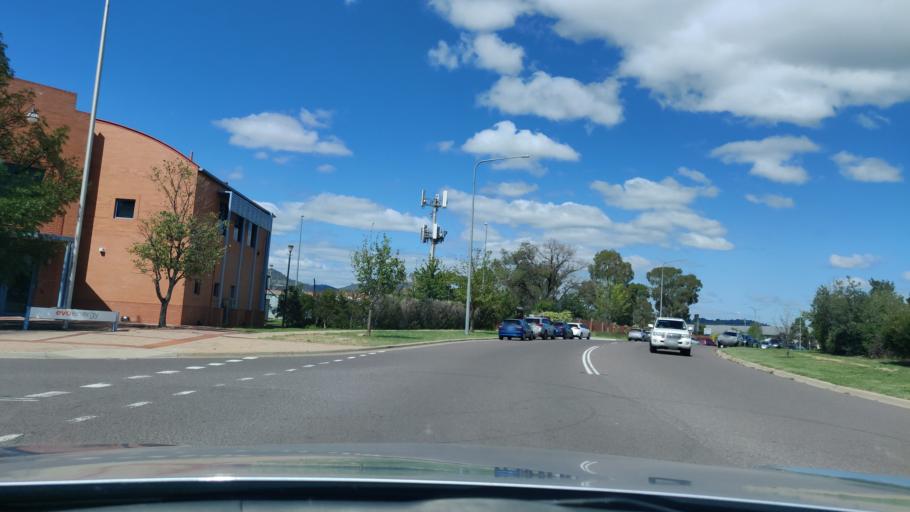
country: AU
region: Australian Capital Territory
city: Macarthur
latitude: -35.4232
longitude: 149.0702
